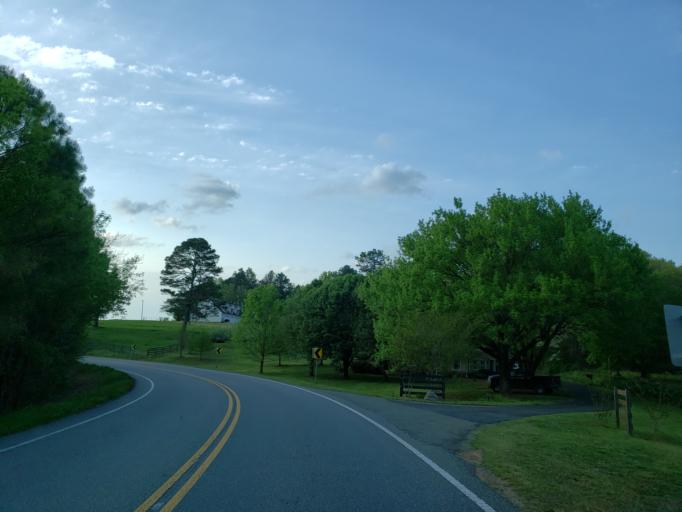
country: US
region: Georgia
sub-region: Cherokee County
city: Ball Ground
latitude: 34.2814
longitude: -84.3754
